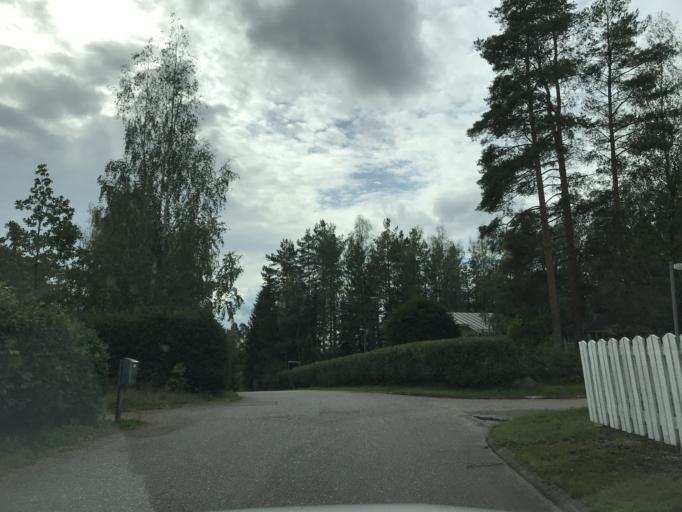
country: FI
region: Paijanne Tavastia
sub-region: Lahti
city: Nastola
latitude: 61.0150
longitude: 25.8141
